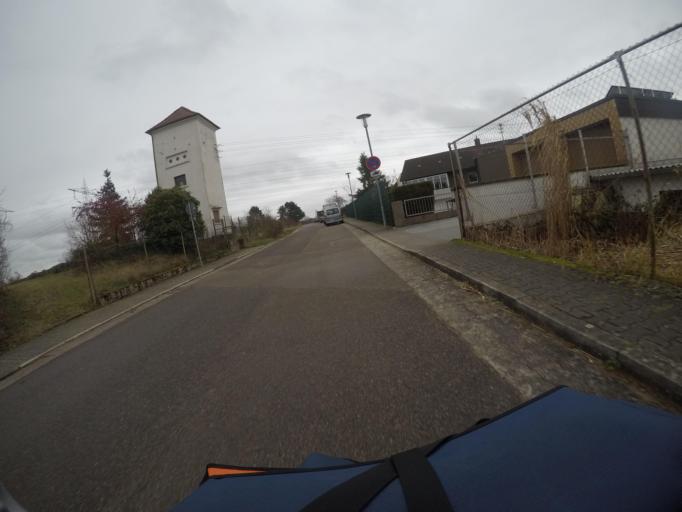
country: DE
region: Baden-Wuerttemberg
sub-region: Karlsruhe Region
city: Philippsburg
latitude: 49.2309
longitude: 8.4687
